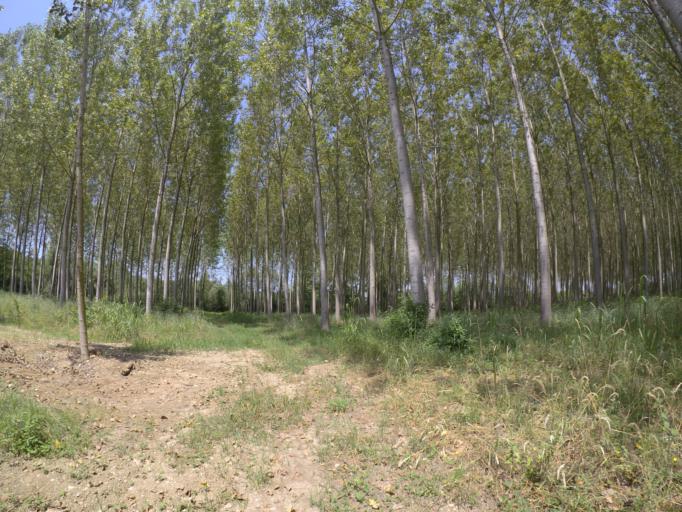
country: IT
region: Friuli Venezia Giulia
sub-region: Provincia di Udine
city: Rivignano
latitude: 45.9107
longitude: 13.0393
